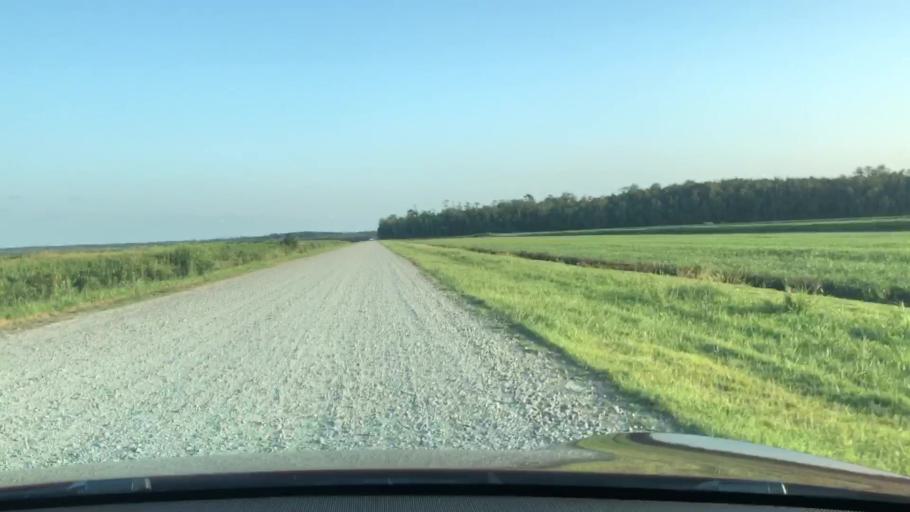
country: US
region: North Carolina
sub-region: Dare County
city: Manteo
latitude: 35.8491
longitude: -75.8613
